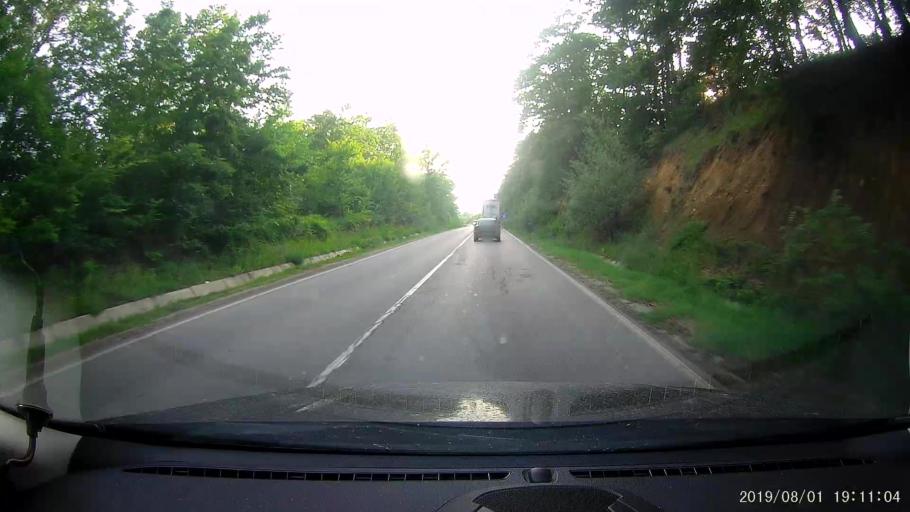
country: BG
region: Shumen
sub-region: Obshtina Smyadovo
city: Smyadovo
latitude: 42.9768
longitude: 26.9656
